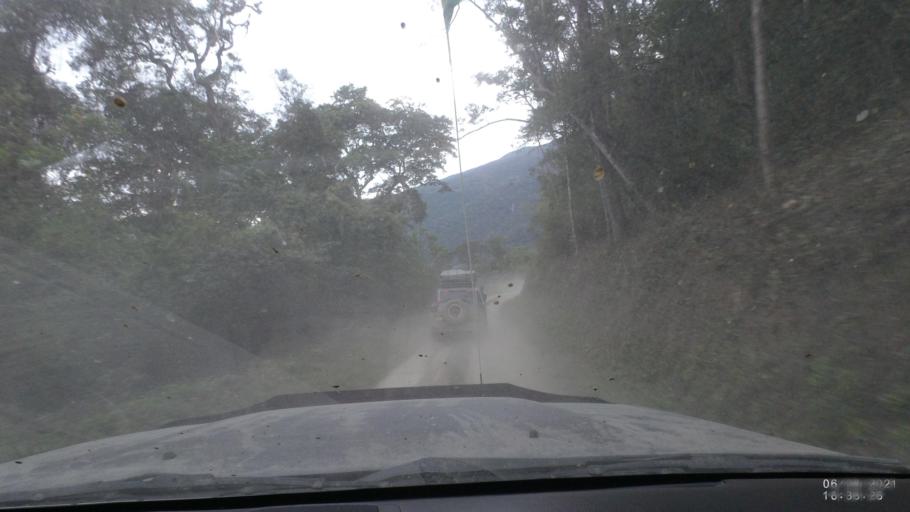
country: BO
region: La Paz
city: Quime
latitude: -16.5152
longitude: -66.7668
